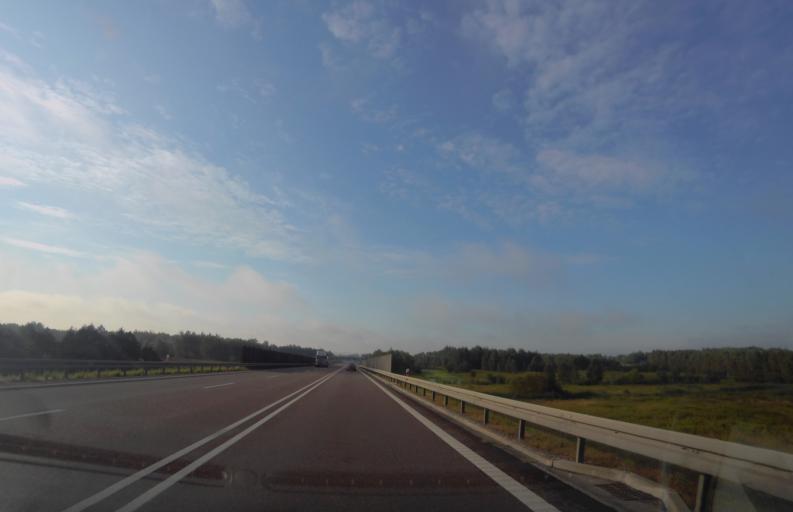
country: PL
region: Subcarpathian Voivodeship
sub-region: Powiat rzeszowski
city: Wolka Podlesna
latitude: 50.1330
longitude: 22.0804
